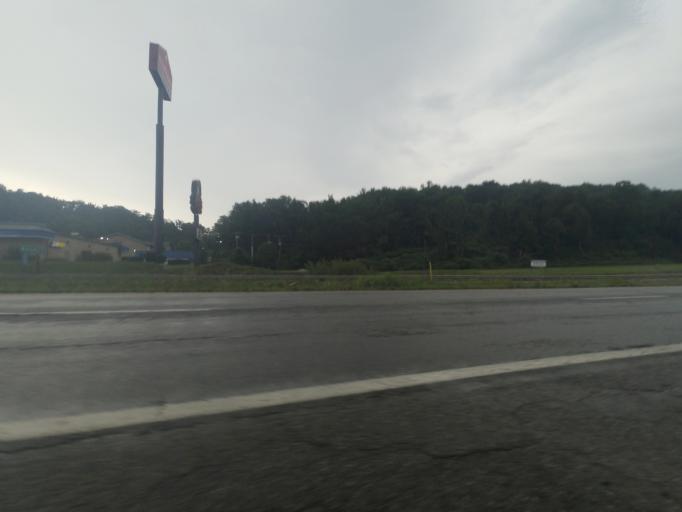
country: US
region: West Virginia
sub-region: Cabell County
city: Huntington
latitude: 38.3949
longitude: -82.4118
